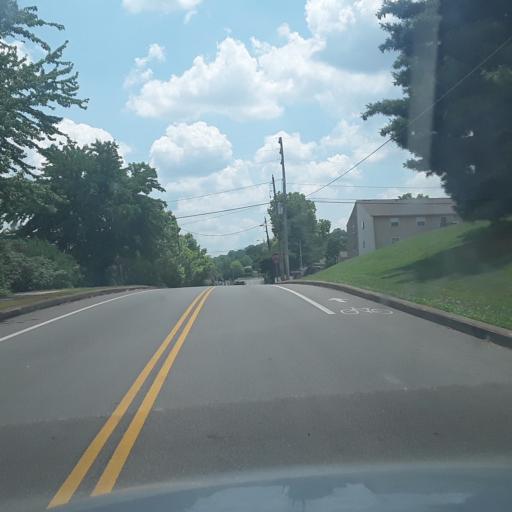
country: US
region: Tennessee
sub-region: Williamson County
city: Brentwood Estates
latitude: 36.0499
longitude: -86.7162
